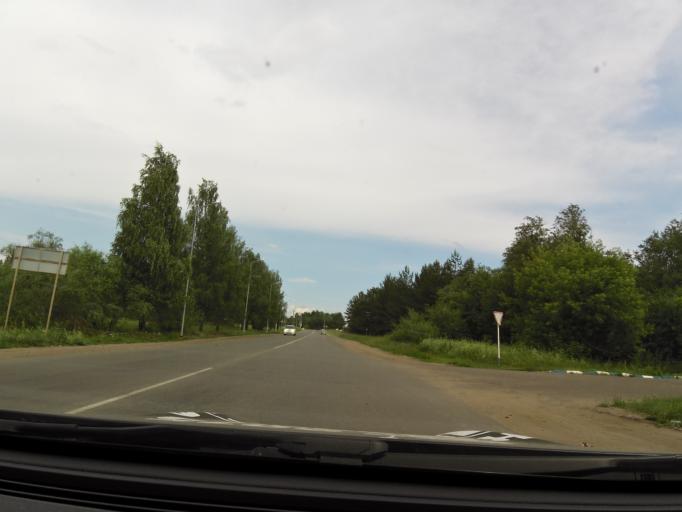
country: RU
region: Kirov
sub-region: Kirovo-Chepetskiy Rayon
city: Kirov
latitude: 58.6170
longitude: 49.7674
